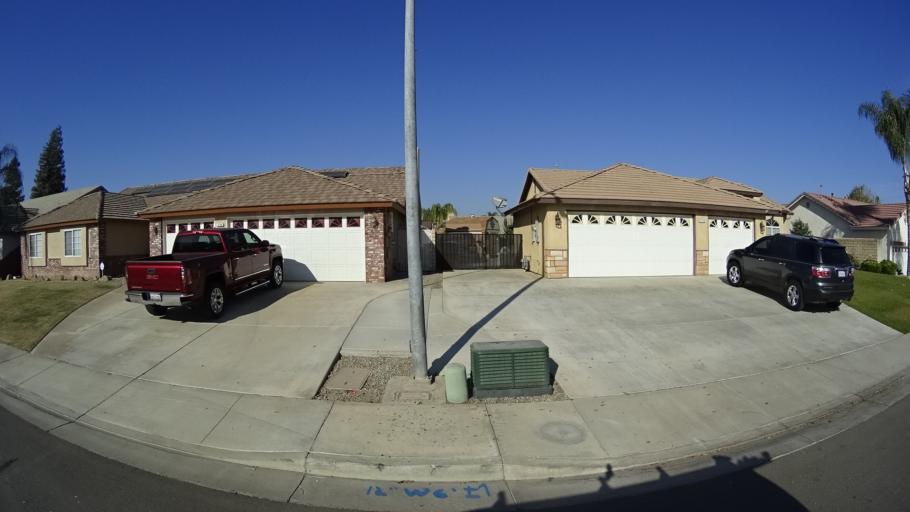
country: US
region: California
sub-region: Kern County
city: Greenfield
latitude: 35.2886
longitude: -119.0368
